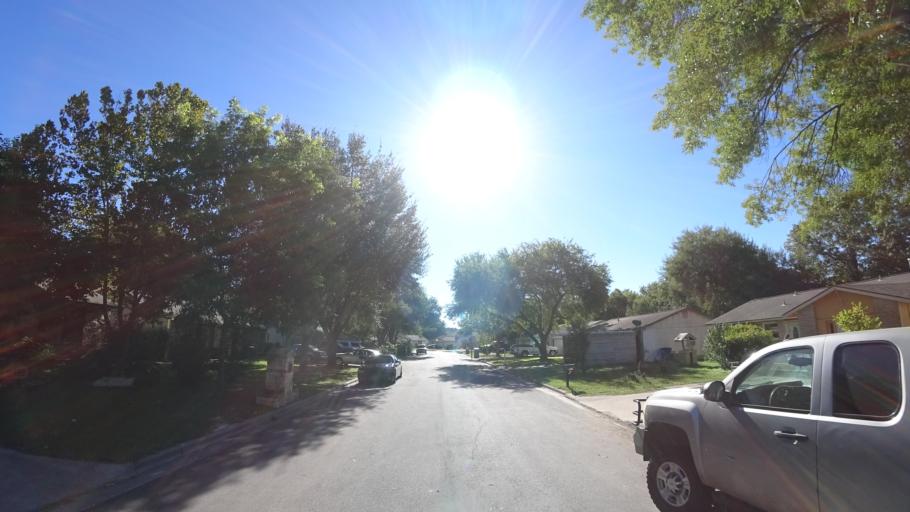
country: US
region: Texas
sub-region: Travis County
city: Hornsby Bend
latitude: 30.3153
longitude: -97.6537
